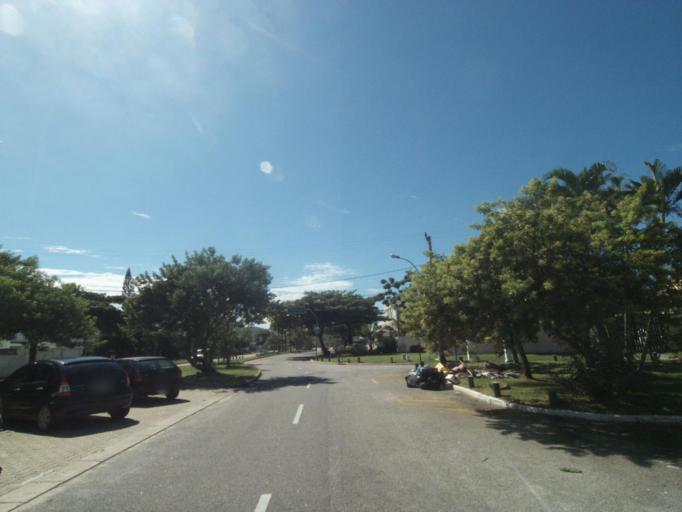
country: BR
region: Rio de Janeiro
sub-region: Niteroi
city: Niteroi
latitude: -22.9574
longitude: -43.0651
